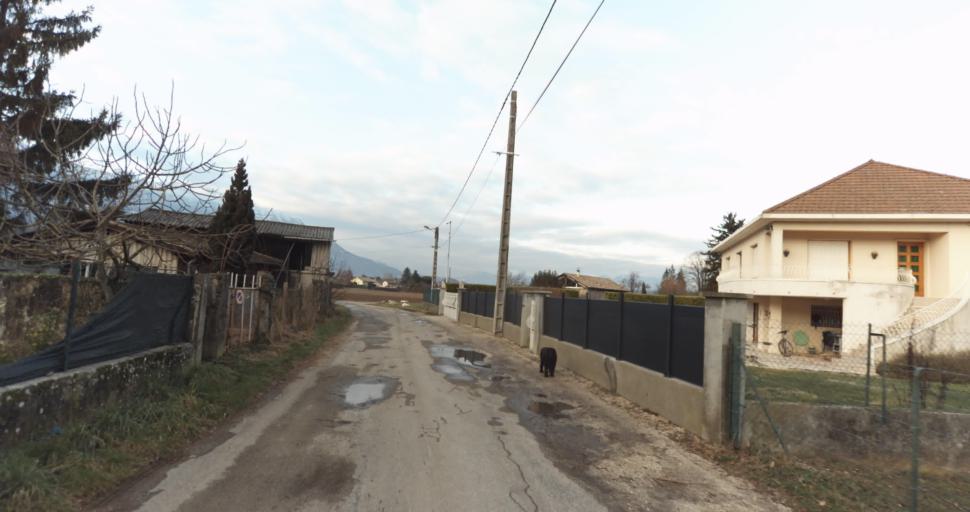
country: FR
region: Rhone-Alpes
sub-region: Departement de l'Isere
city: Vif
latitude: 45.0685
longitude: 5.6973
